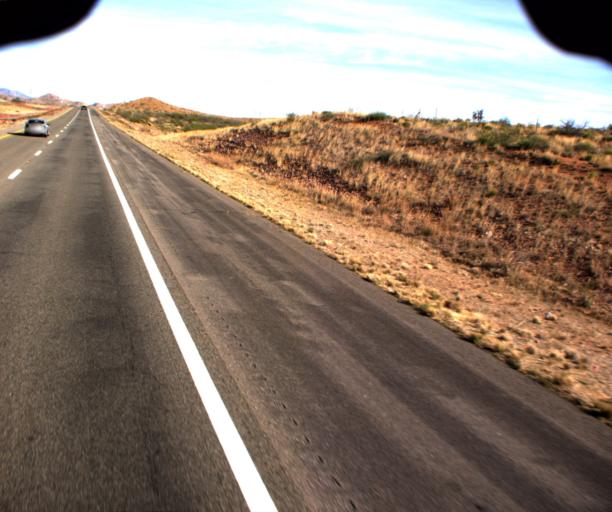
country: US
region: Arizona
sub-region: Cochise County
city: Willcox
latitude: 32.4604
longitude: -109.6670
